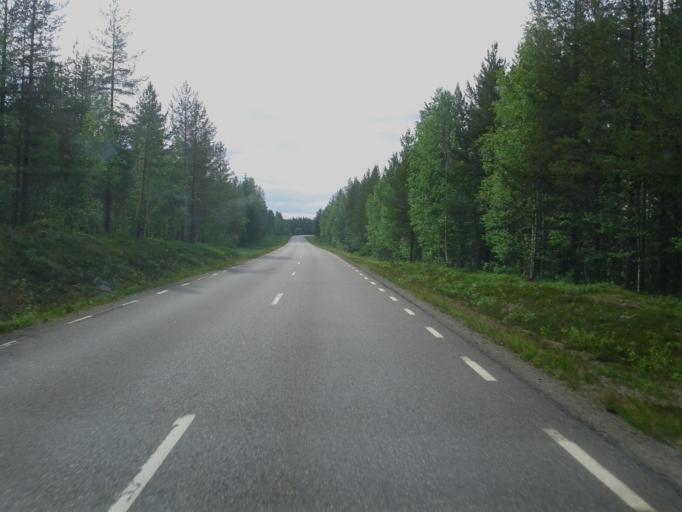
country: SE
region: Vaesterbotten
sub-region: Lycksele Kommun
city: Soderfors
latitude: 65.2561
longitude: 18.2290
